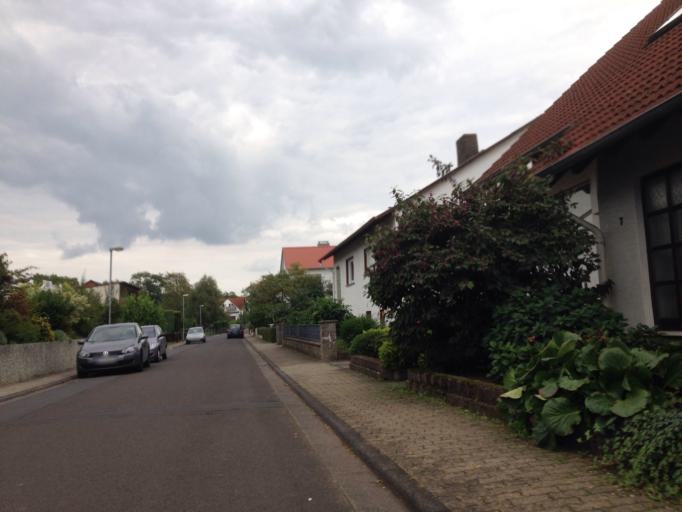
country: DE
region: Hesse
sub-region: Regierungsbezirk Giessen
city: Alten Buseck
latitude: 50.6188
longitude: 8.7567
